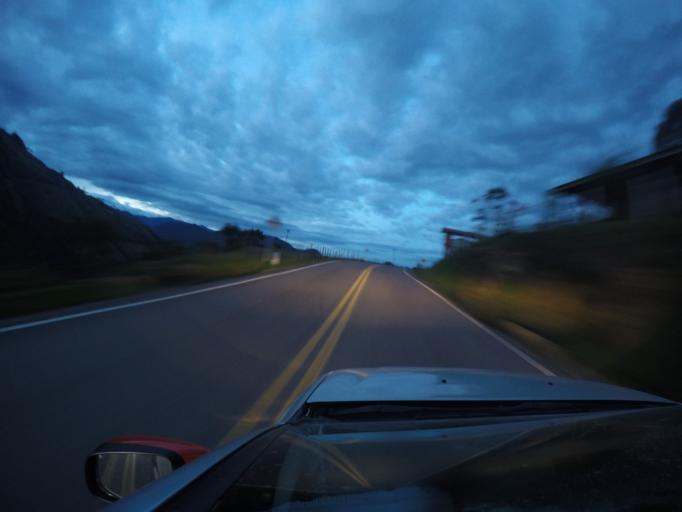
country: CO
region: Tolima
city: Casabianca
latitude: 5.1367
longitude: -75.1375
